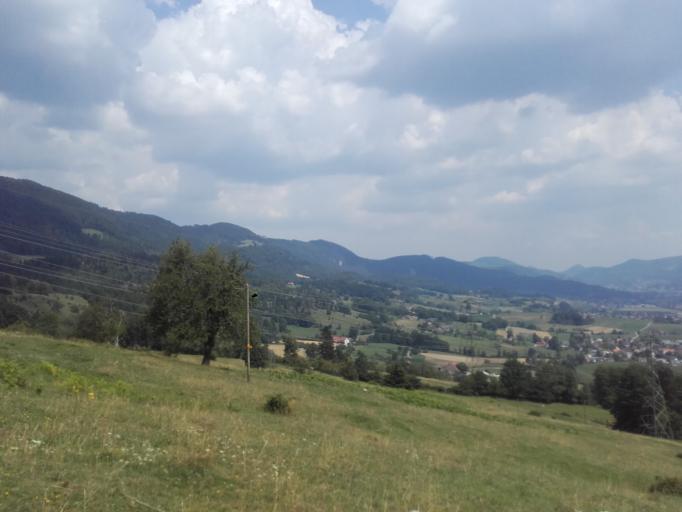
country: CH
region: Solothurn
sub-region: Bezirk Thal
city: Matzendorf
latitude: 47.3033
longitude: 7.5886
